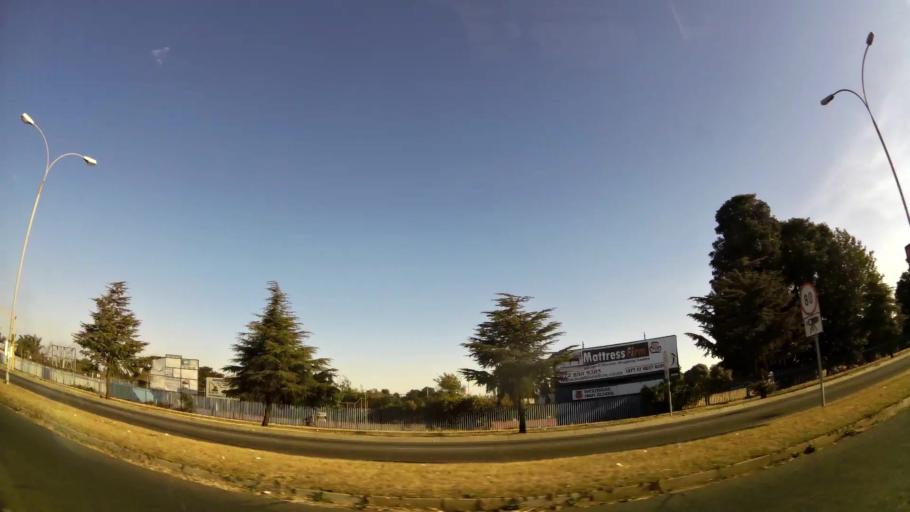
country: ZA
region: Gauteng
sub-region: City of Johannesburg Metropolitan Municipality
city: Roodepoort
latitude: -26.1430
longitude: 27.8751
